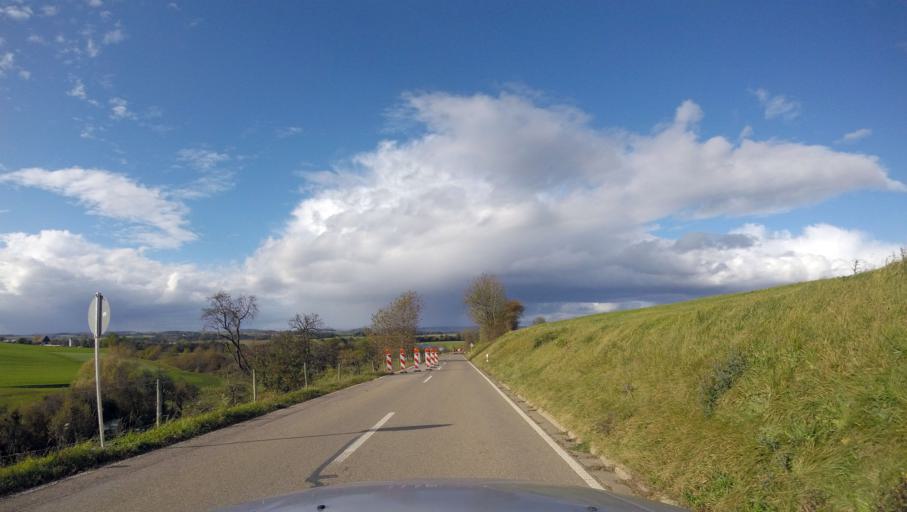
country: DE
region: Baden-Wuerttemberg
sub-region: Regierungsbezirk Stuttgart
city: Ottenbach
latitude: 48.7550
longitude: 9.7397
